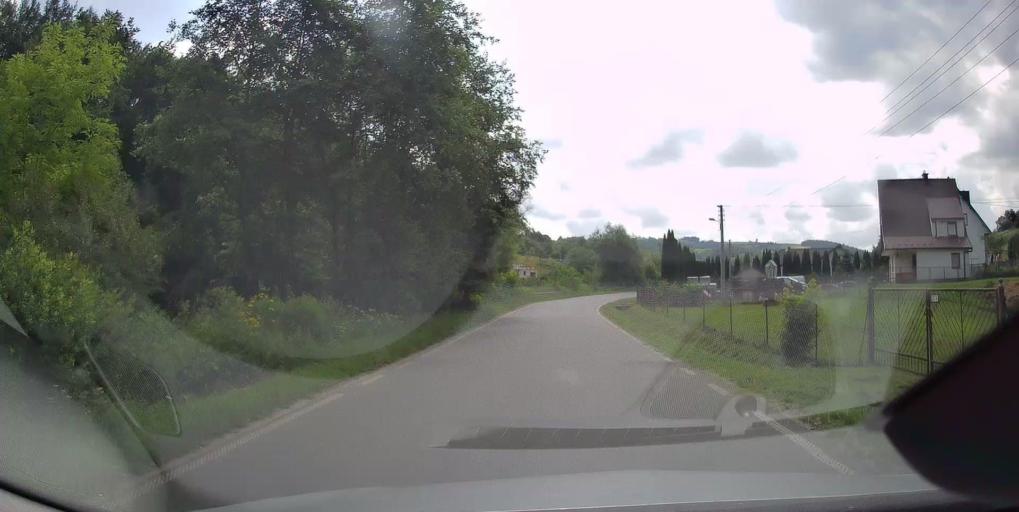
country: PL
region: Lesser Poland Voivodeship
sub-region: Powiat nowosadecki
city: Korzenna
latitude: 49.7412
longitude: 20.7689
